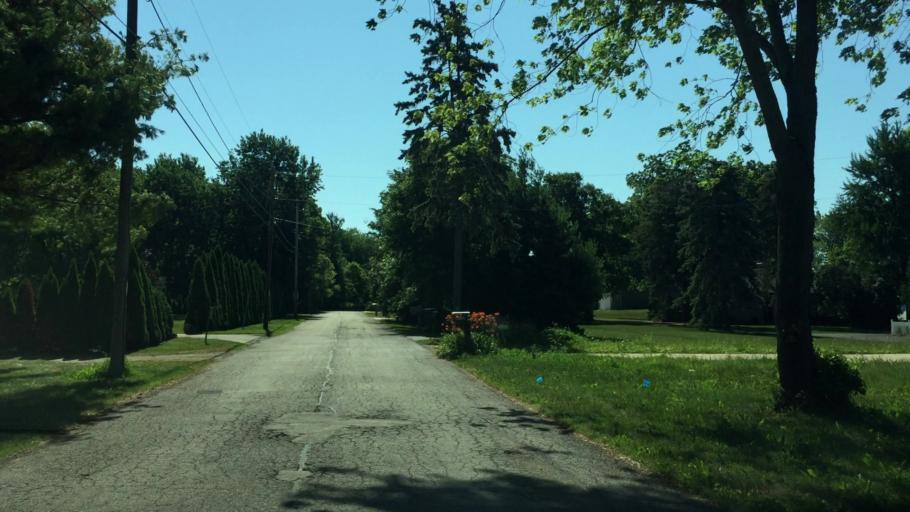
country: US
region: Wisconsin
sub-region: Outagamie County
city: Kimberly
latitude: 44.2046
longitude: -88.3617
